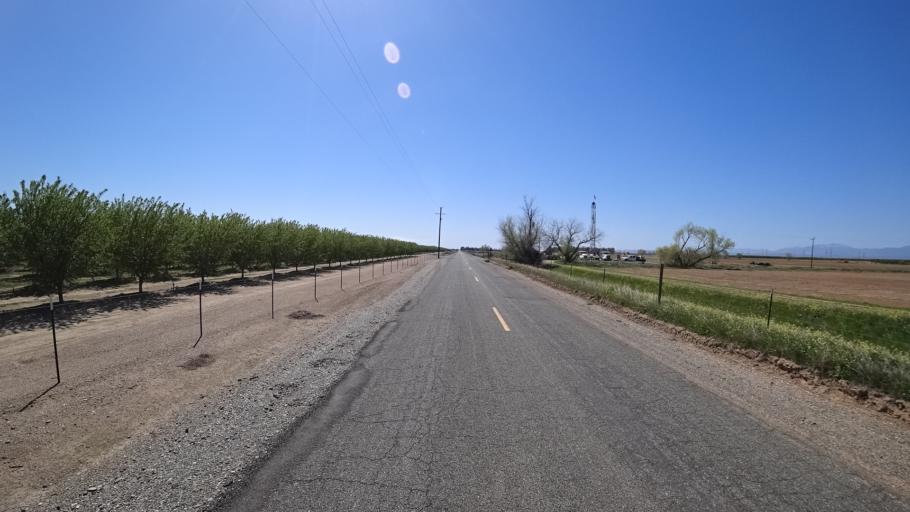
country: US
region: California
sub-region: Glenn County
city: Orland
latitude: 39.6945
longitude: -122.2530
